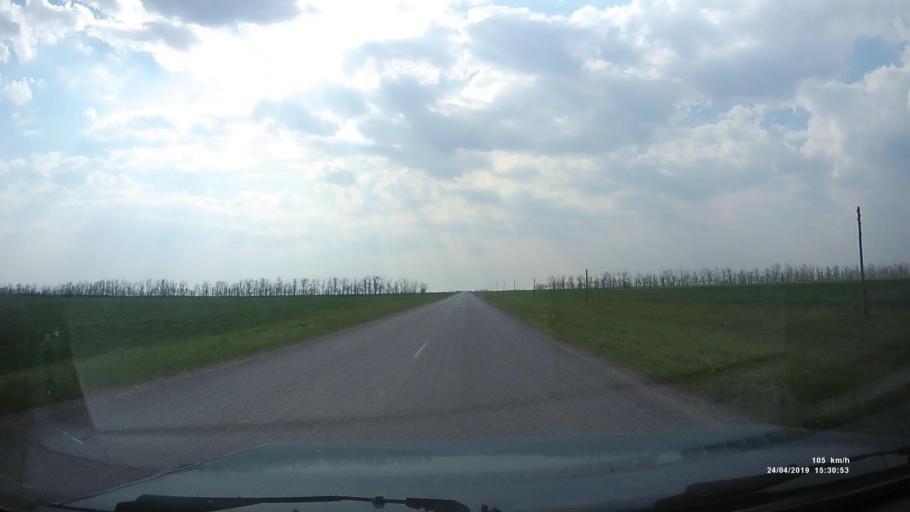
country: RU
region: Rostov
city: Remontnoye
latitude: 46.5996
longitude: 42.9975
